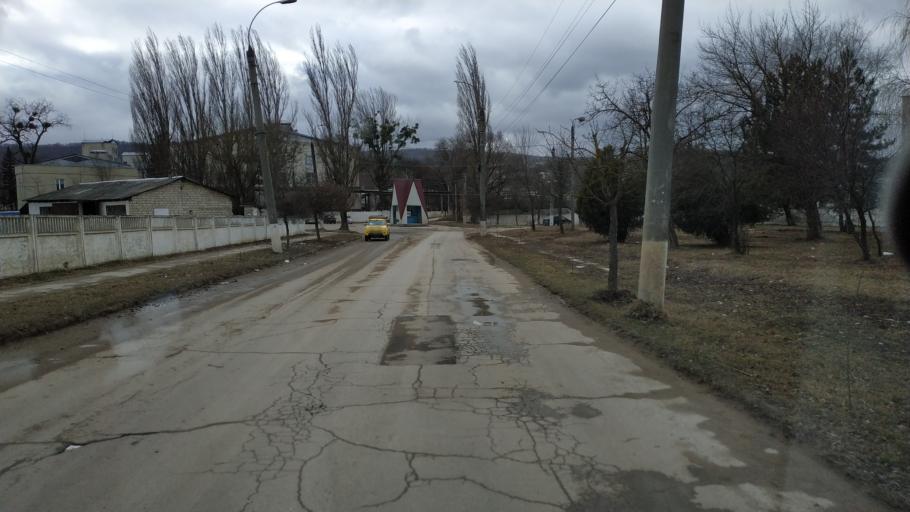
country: MD
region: Calarasi
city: Calarasi
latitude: 47.2438
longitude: 28.3141
